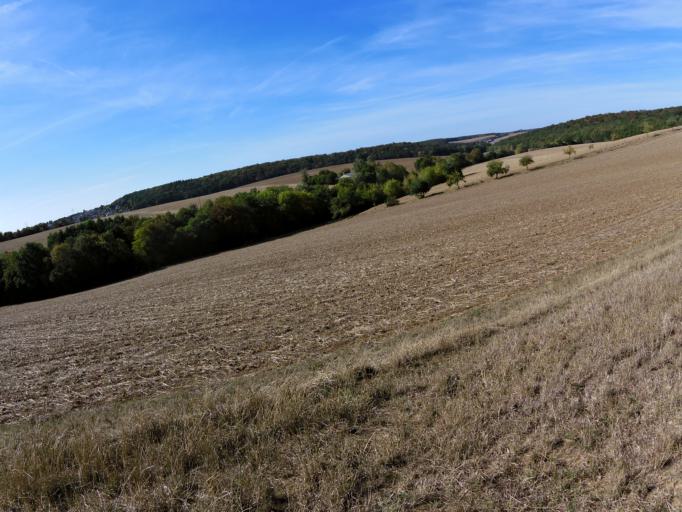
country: DE
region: Bavaria
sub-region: Regierungsbezirk Unterfranken
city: Eisingen
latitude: 49.7650
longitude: 9.8226
